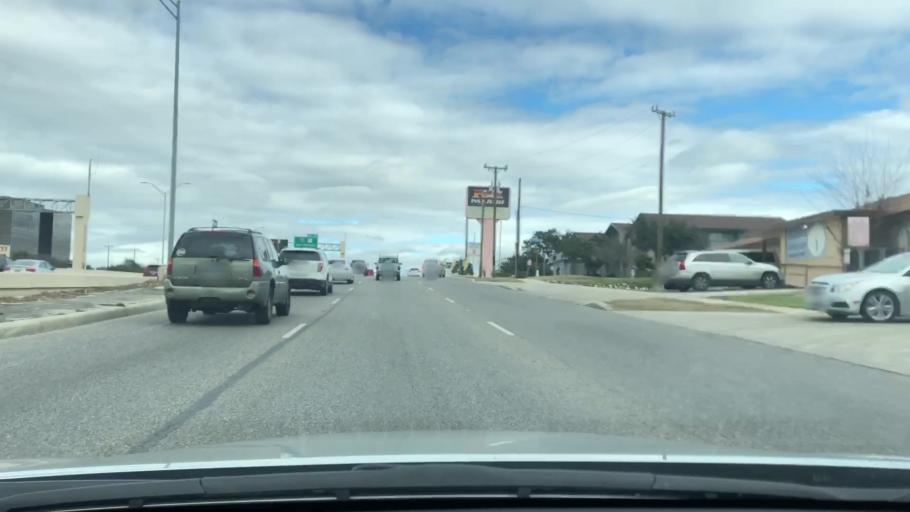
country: US
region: Texas
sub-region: Bexar County
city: Balcones Heights
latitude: 29.4876
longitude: -98.5847
